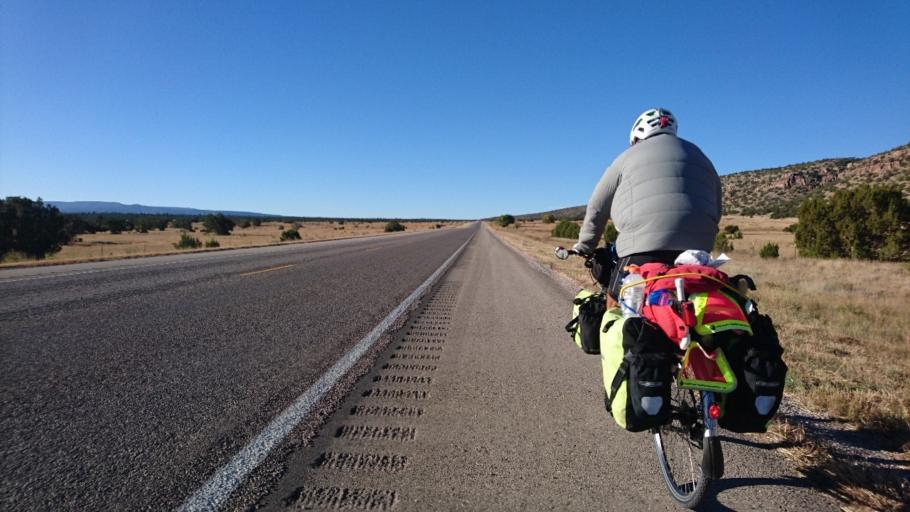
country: US
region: New Mexico
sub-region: Cibola County
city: Grants
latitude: 34.9929
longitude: -107.8997
